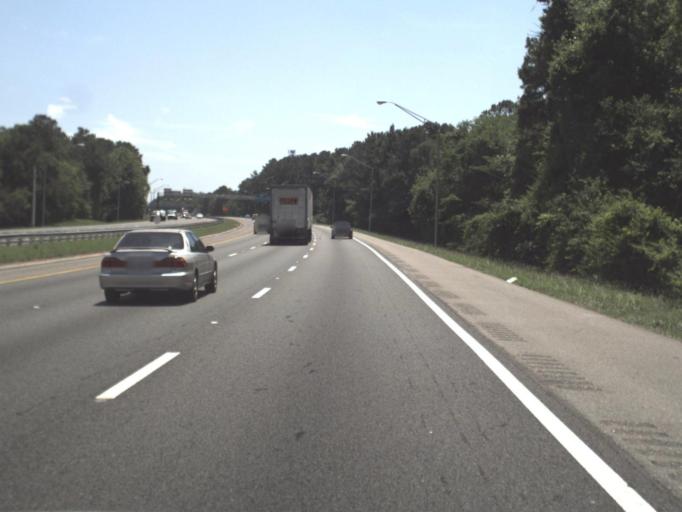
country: US
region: Florida
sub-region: Clay County
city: Bellair-Meadowbrook Terrace
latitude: 30.2839
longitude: -81.7719
